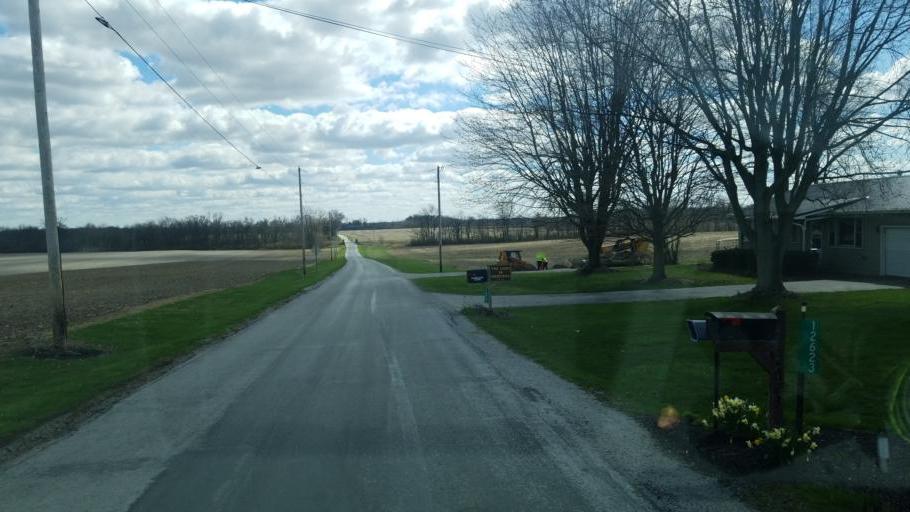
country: US
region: Ohio
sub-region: Hardin County
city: Kenton
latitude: 40.6374
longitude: -83.5619
